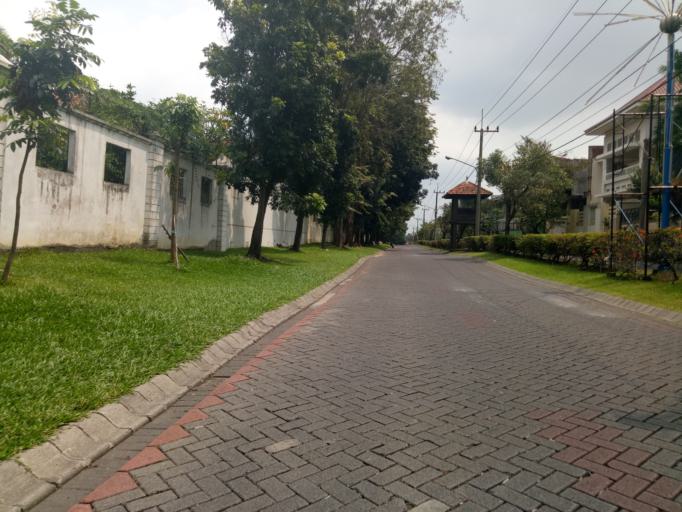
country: ID
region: East Java
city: Jagirsidosermo
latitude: -7.2938
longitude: 112.6917
